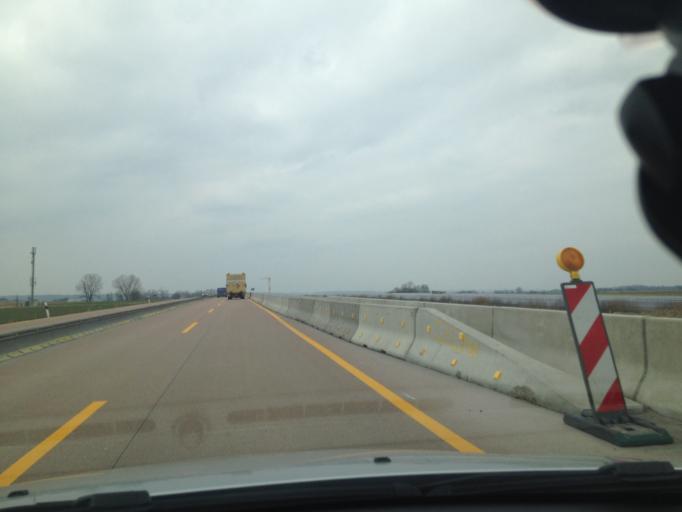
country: DE
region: Bavaria
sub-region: Swabia
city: Rosshaupten
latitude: 48.4112
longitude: 10.4823
